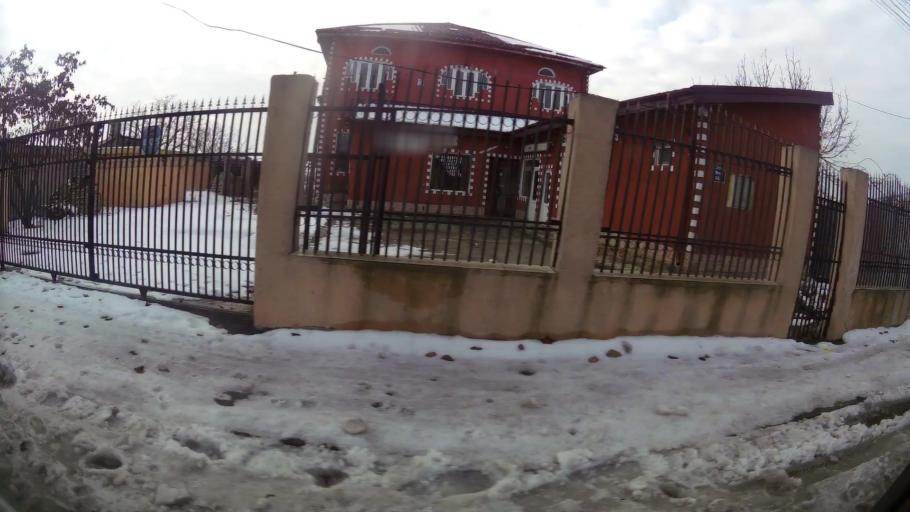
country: RO
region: Ilfov
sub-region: Comuna Glina
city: Catelu
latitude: 44.4023
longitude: 26.2147
